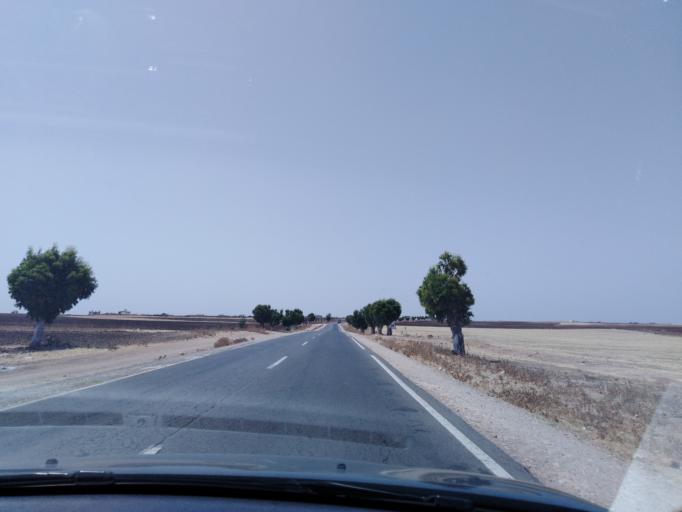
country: MA
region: Doukkala-Abda
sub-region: Safi
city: Youssoufia
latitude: 32.3835
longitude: -8.8253
